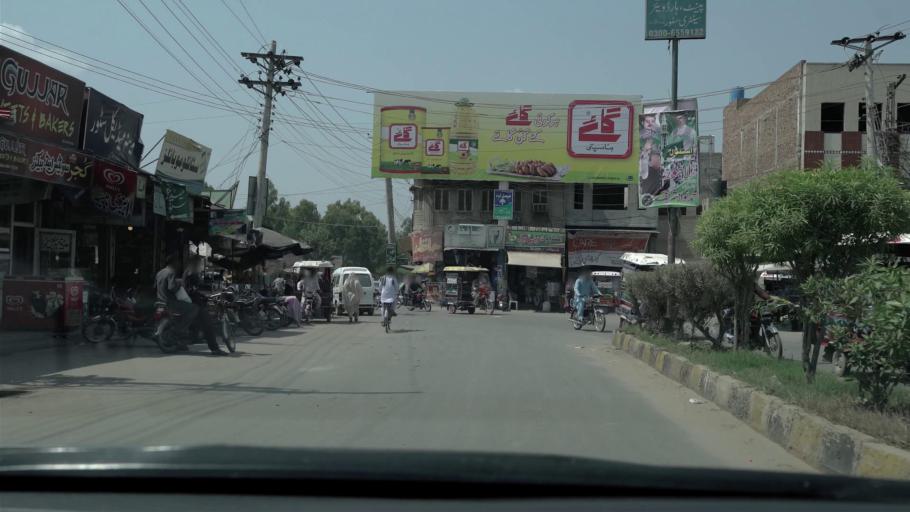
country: PK
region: Punjab
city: Gojra
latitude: 31.1520
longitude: 72.6771
